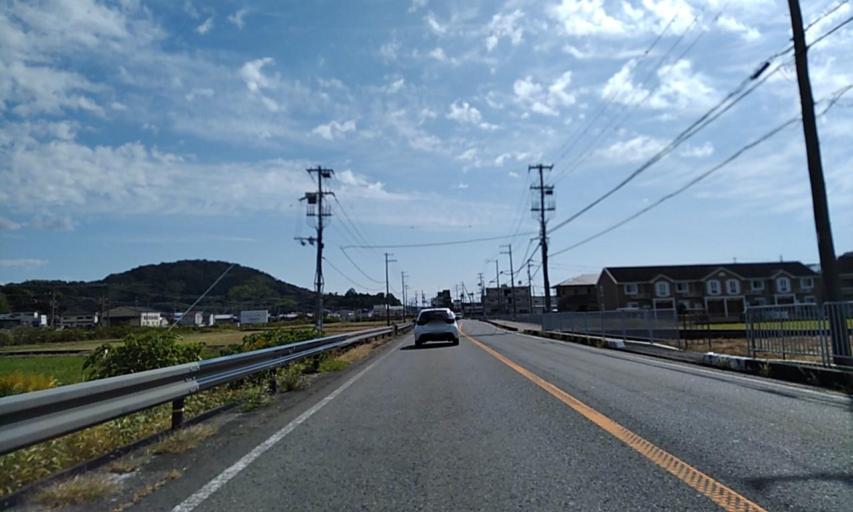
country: JP
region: Wakayama
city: Gobo
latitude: 33.9208
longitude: 135.1461
